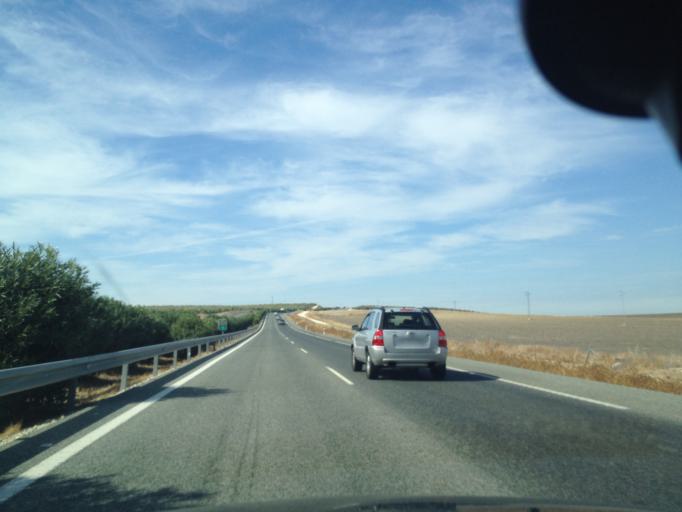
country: ES
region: Andalusia
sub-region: Provincia de Sevilla
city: Osuna
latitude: 37.2332
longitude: -5.1991
